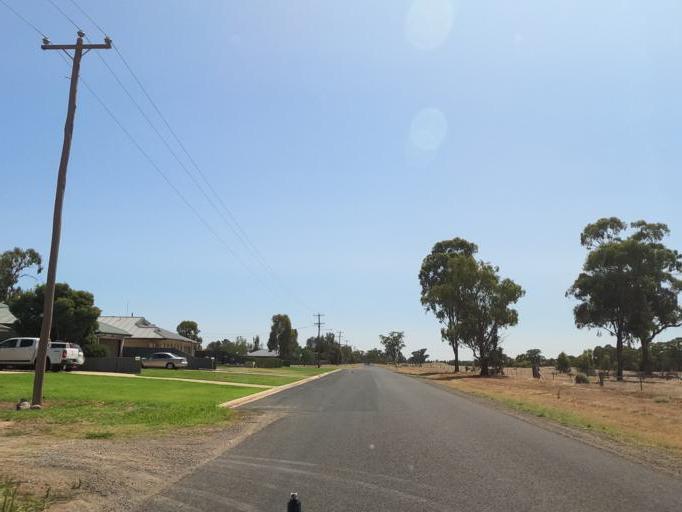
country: AU
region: New South Wales
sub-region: Corowa Shire
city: Mulwala
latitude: -35.9831
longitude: 146.0010
